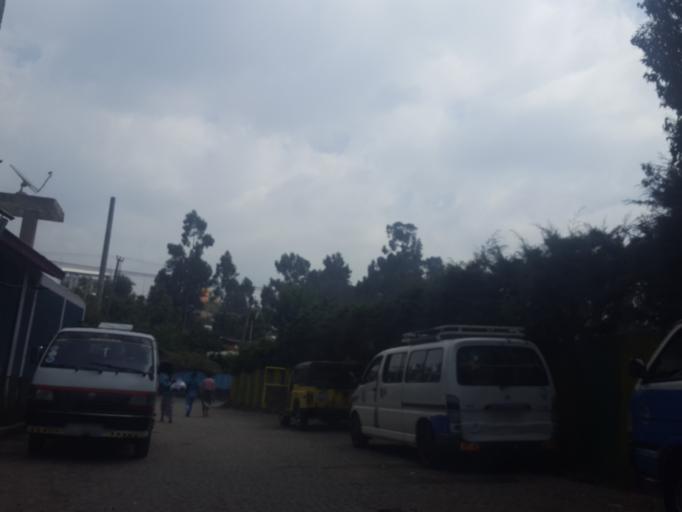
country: ET
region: Adis Abeba
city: Addis Ababa
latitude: 9.0636
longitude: 38.7265
